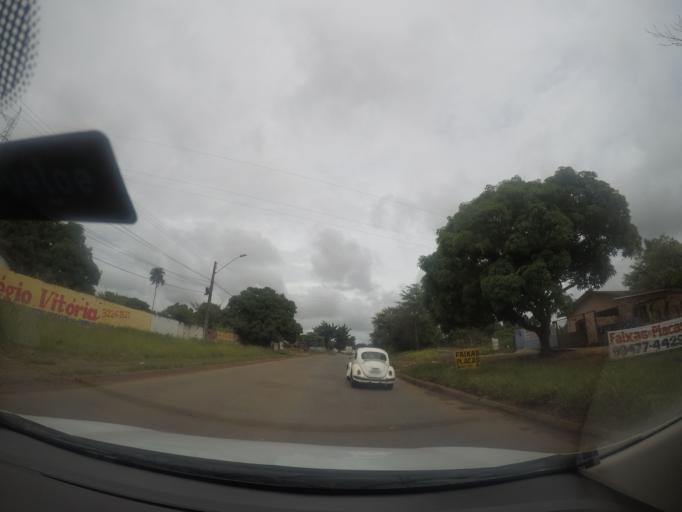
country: BR
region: Goias
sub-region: Goiania
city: Goiania
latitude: -16.6843
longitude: -49.3610
